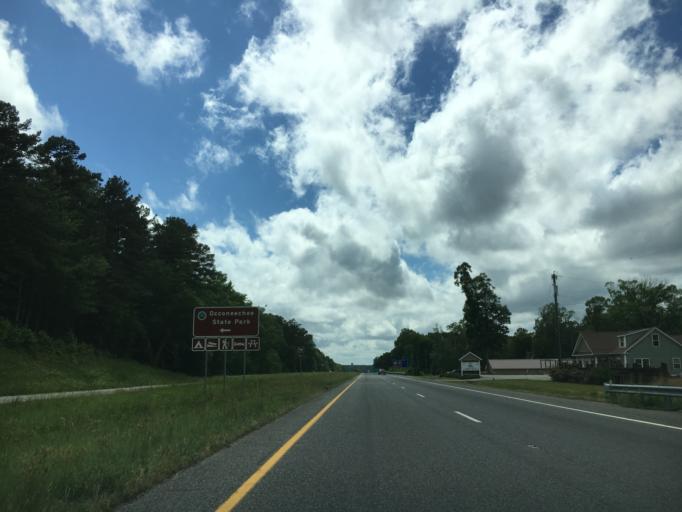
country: US
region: Virginia
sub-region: Mecklenburg County
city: Clarksville
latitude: 36.6370
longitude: -78.5252
